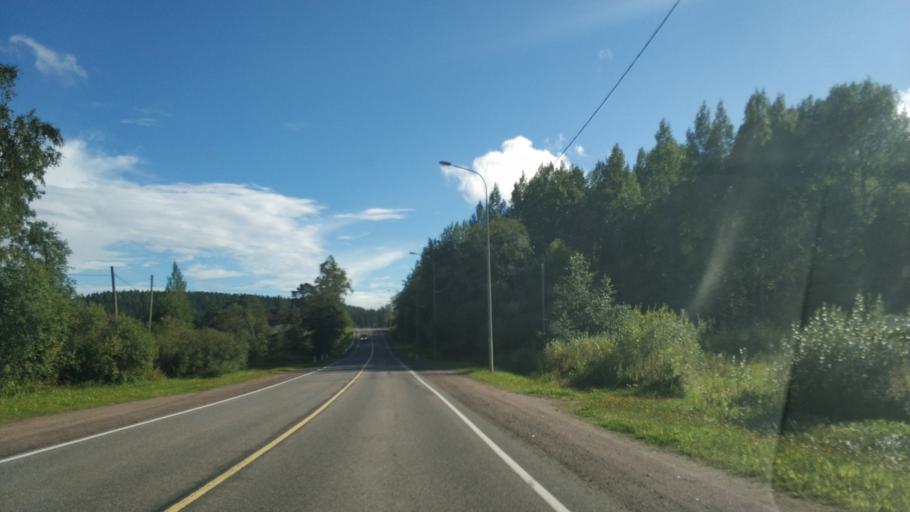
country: RU
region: Republic of Karelia
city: Sortavala
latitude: 61.6661
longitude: 30.6540
